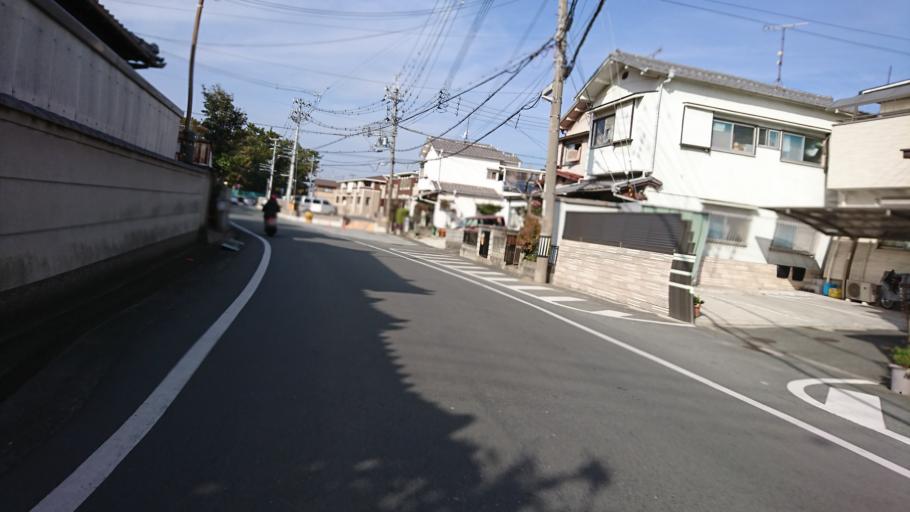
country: JP
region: Hyogo
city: Kakogawacho-honmachi
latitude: 34.7375
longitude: 134.8367
